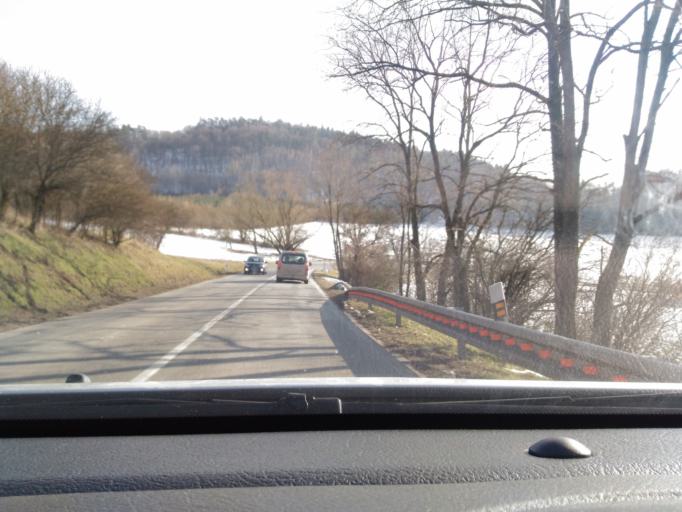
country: CZ
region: South Moravian
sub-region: Okres Brno-Venkov
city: Dolni Loucky
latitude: 49.4096
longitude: 16.3518
